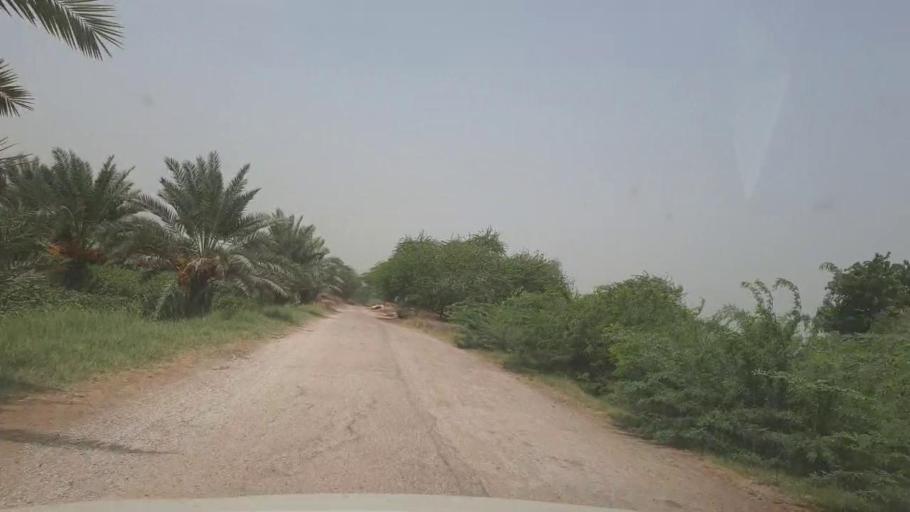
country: PK
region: Sindh
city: Kot Diji
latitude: 27.3653
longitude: 68.6565
